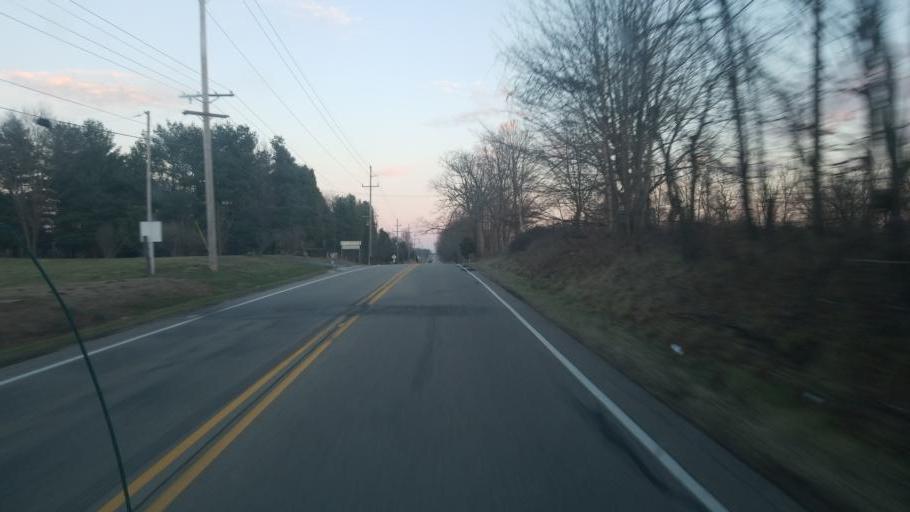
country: US
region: Indiana
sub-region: Lawrence County
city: Bedford
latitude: 38.8754
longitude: -86.3923
